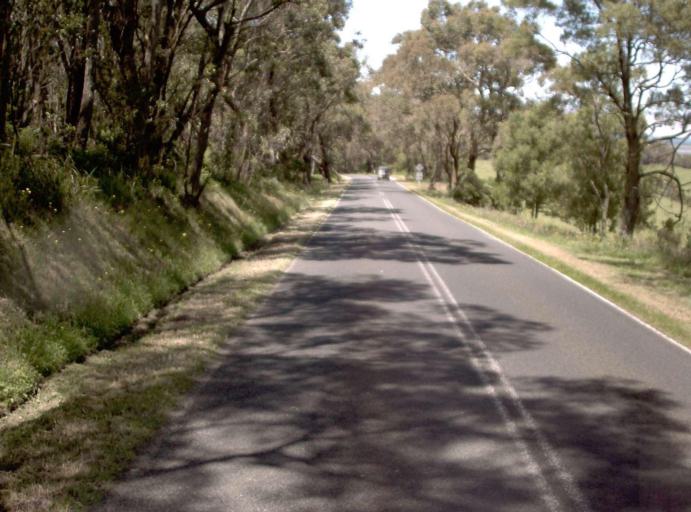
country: AU
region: Victoria
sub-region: Bass Coast
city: North Wonthaggi
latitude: -38.7401
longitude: 146.1286
